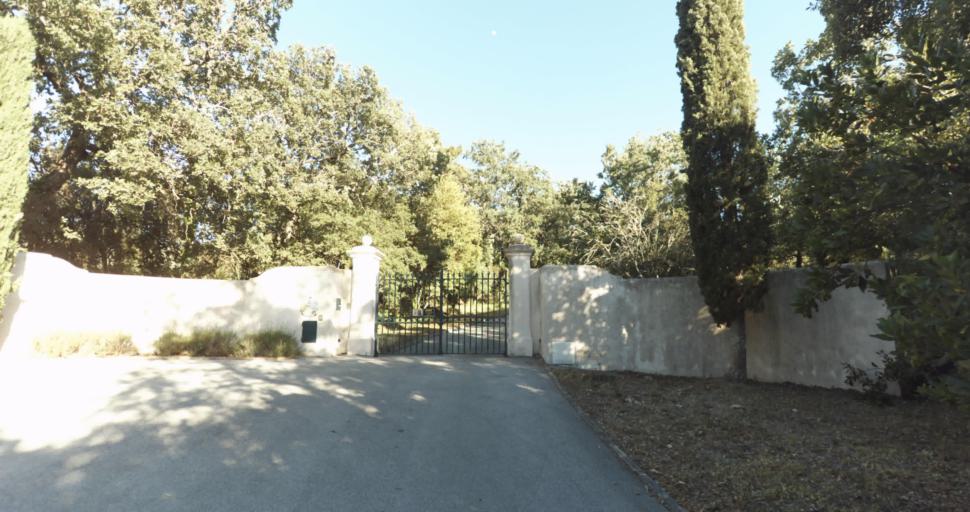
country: FR
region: Provence-Alpes-Cote d'Azur
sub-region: Departement du Var
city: Gassin
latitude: 43.2302
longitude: 6.5956
